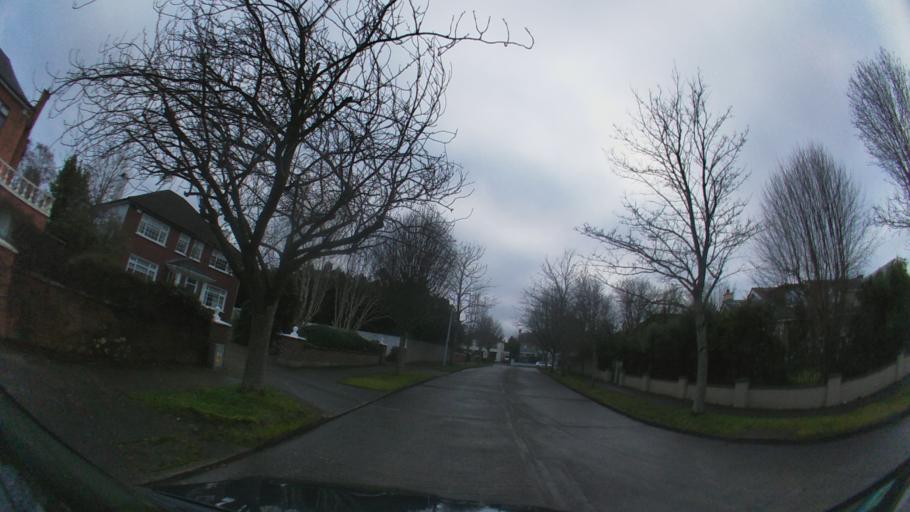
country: IE
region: Leinster
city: Castleknock
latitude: 53.3712
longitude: -6.3611
